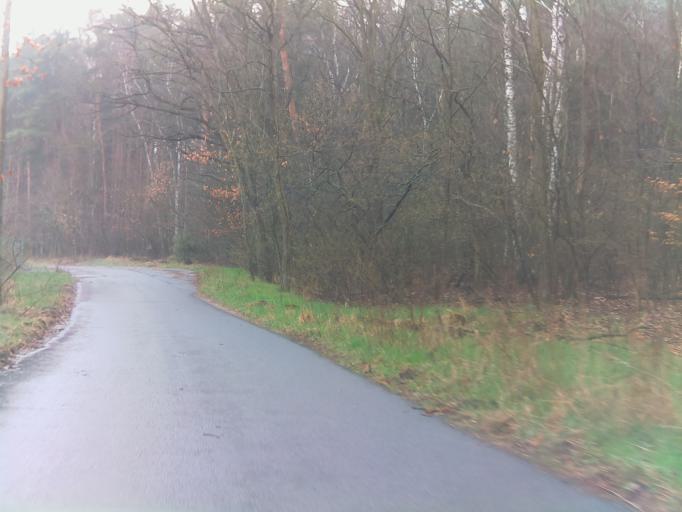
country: DE
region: Brandenburg
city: Jamlitz
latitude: 52.0408
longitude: 14.3699
